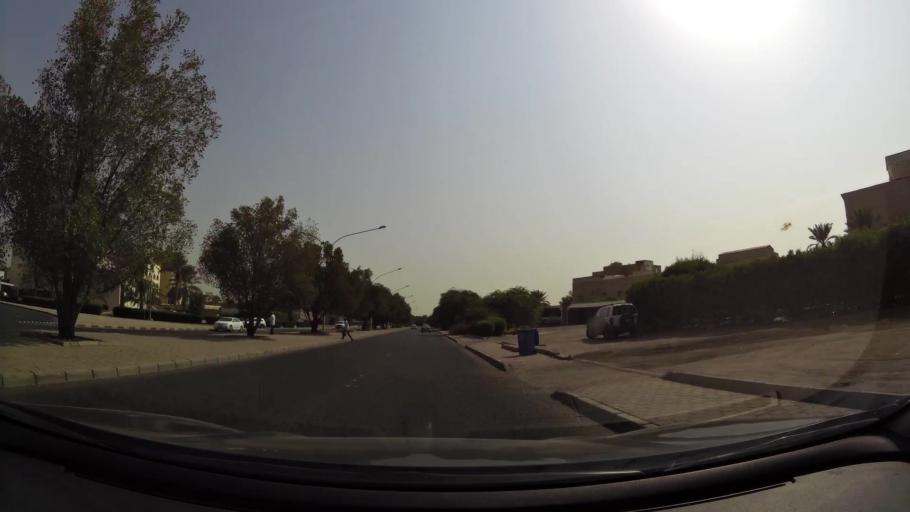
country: KW
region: Al Asimah
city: Ar Rabiyah
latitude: 29.2890
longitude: 47.8965
